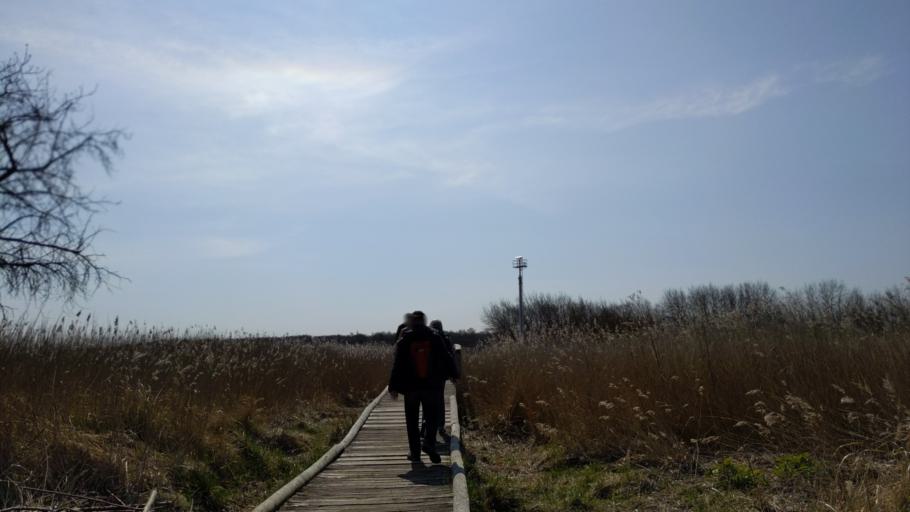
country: DE
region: Schleswig-Holstein
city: Travemuende
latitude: 53.9420
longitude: 10.8693
